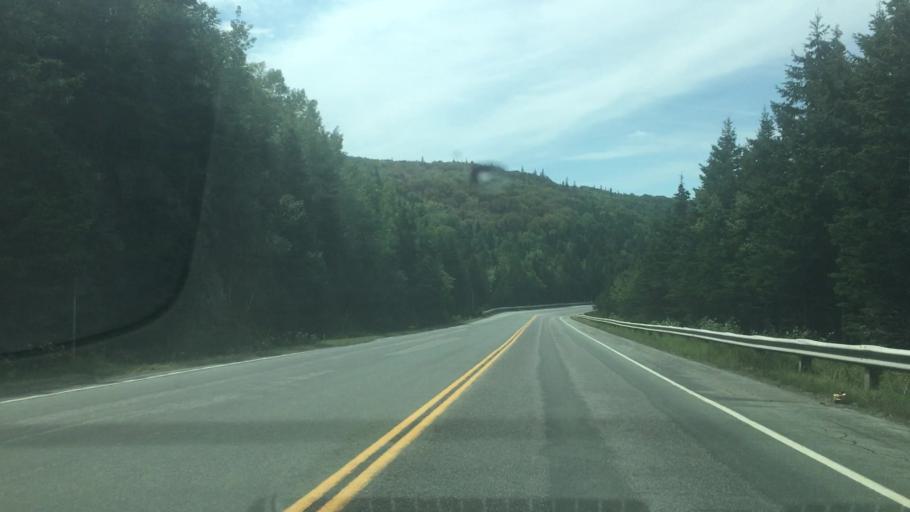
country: CA
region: Nova Scotia
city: Sydney Mines
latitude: 46.2421
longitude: -60.5600
